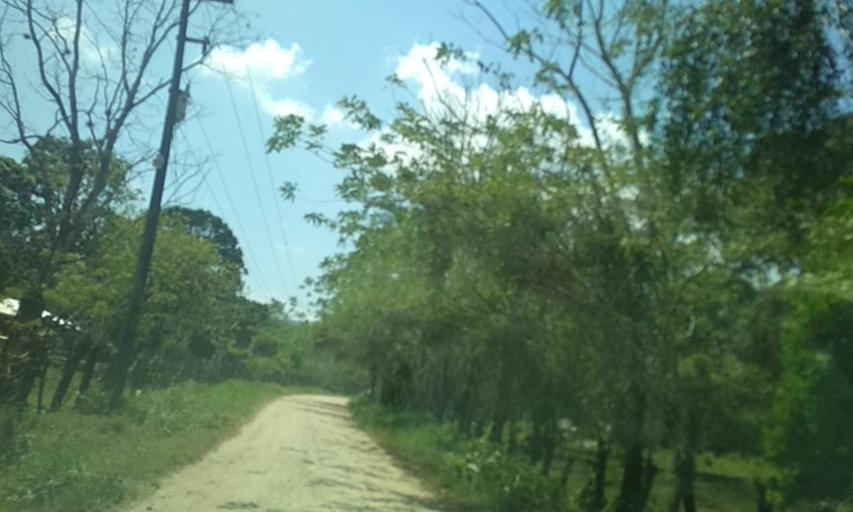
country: MX
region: Chiapas
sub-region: Tecpatan
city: Raudales Malpaso
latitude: 17.2838
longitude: -93.8344
